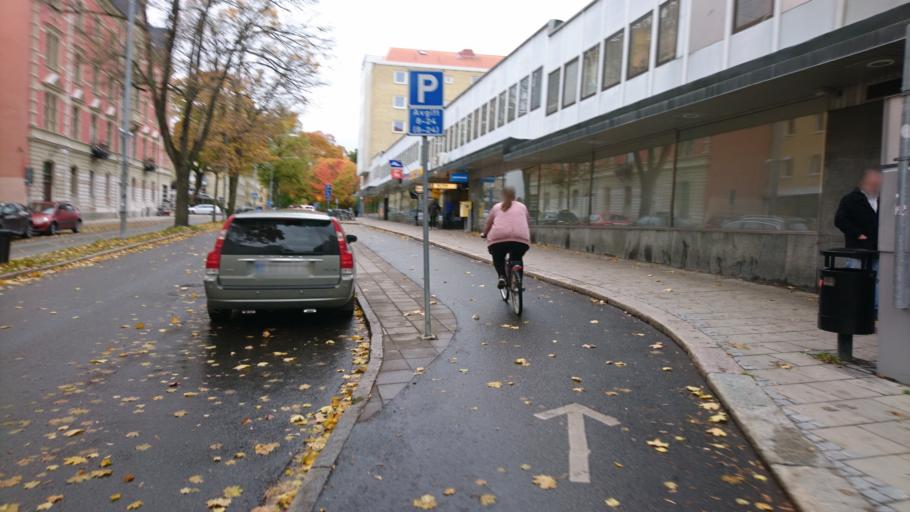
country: SE
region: Uppsala
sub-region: Uppsala Kommun
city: Uppsala
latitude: 59.8611
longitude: 17.6295
